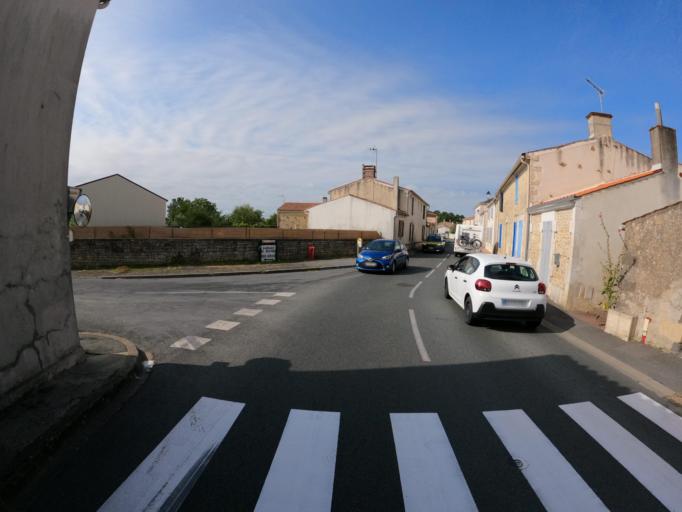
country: FR
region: Pays de la Loire
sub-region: Departement de la Vendee
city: Triaize
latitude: 46.3556
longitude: -1.2464
